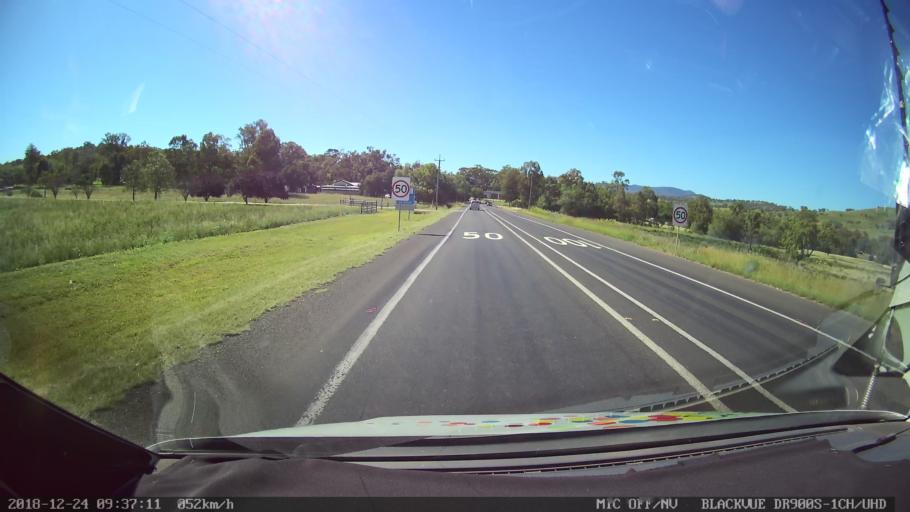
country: AU
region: New South Wales
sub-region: Liverpool Plains
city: Quirindi
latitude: -31.6432
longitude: 150.7247
